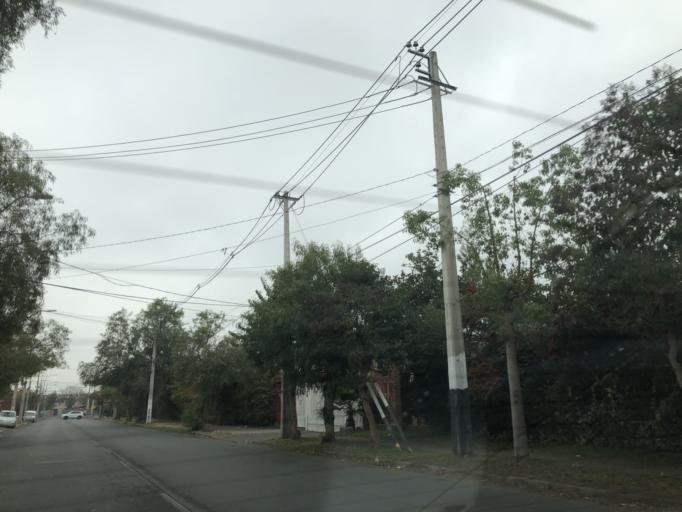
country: CL
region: Santiago Metropolitan
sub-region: Provincia de Cordillera
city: Puente Alto
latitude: -33.5865
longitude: -70.5887
